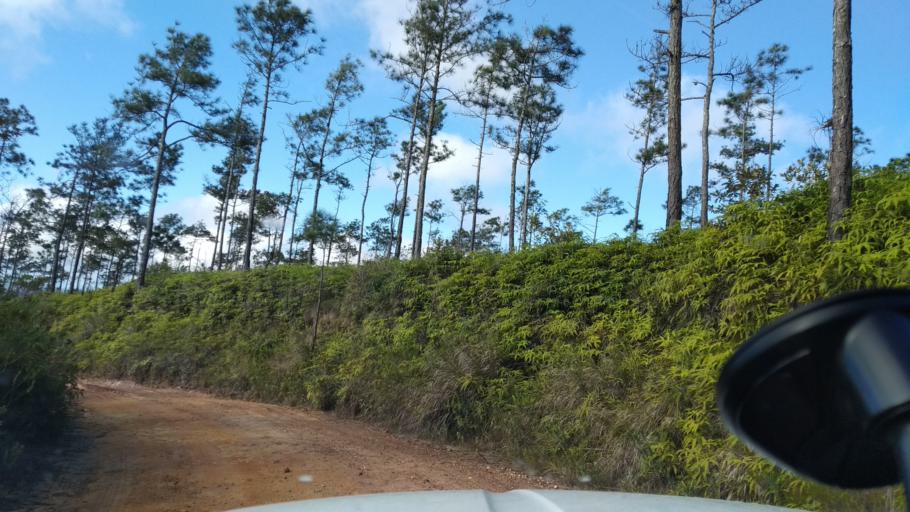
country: BZ
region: Cayo
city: Belmopan
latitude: 16.9983
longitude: -88.8320
